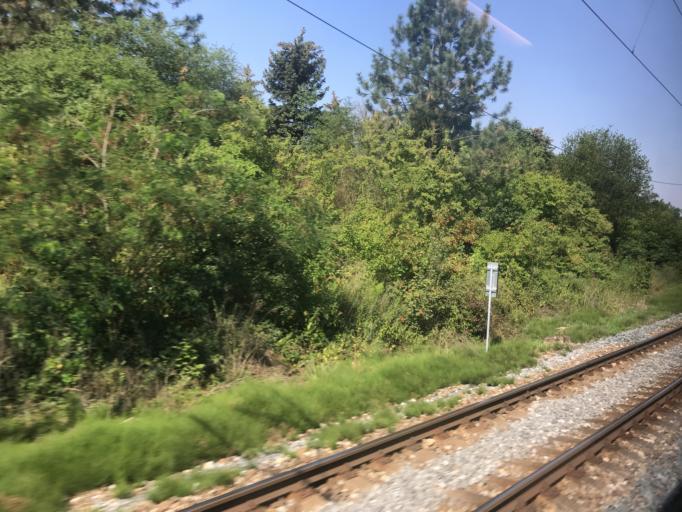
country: CZ
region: Praha
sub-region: Praha 9
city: Vysocany
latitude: 50.0601
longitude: 14.5202
